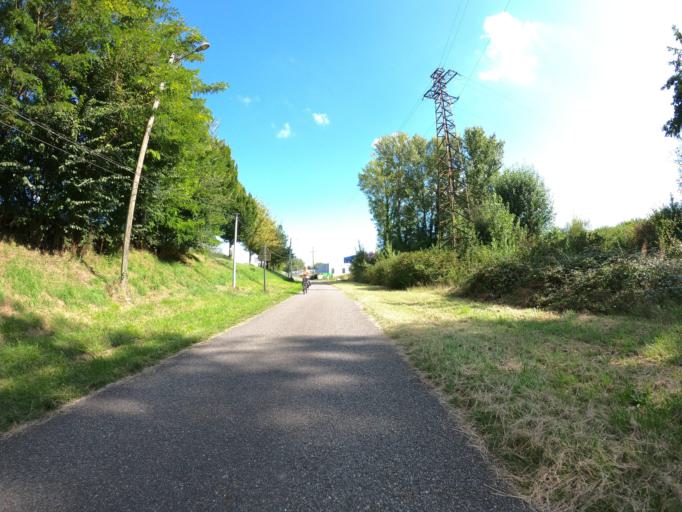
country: FR
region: Midi-Pyrenees
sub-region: Departement du Tarn-et-Garonne
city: Saint-Nicolas-de-la-Grave
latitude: 44.0844
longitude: 0.9768
